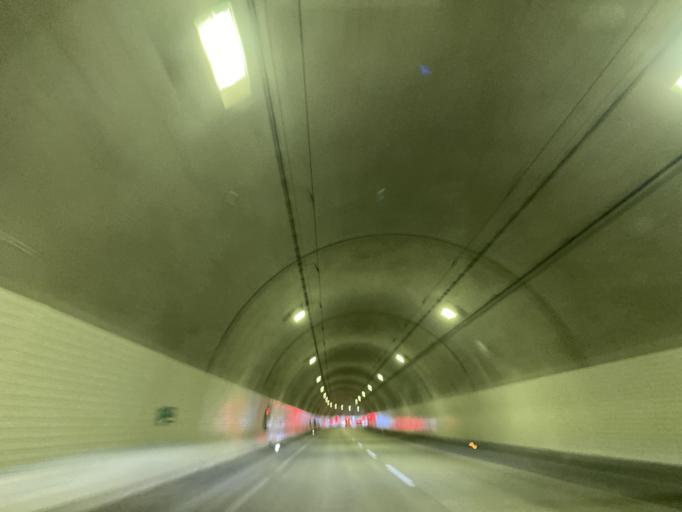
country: JP
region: Miyagi
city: Sendai-shi
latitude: 38.2851
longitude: 140.8565
